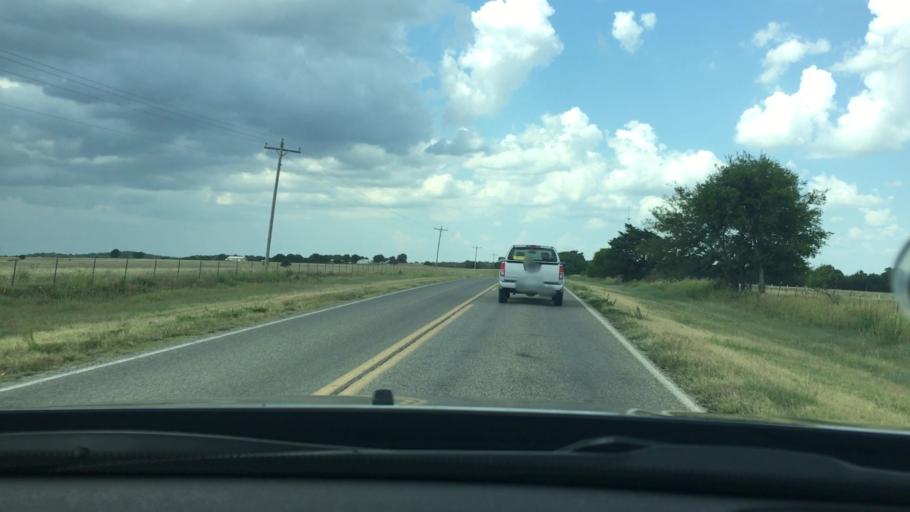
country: US
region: Oklahoma
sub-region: Pontotoc County
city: Ada
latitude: 34.5529
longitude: -96.6347
